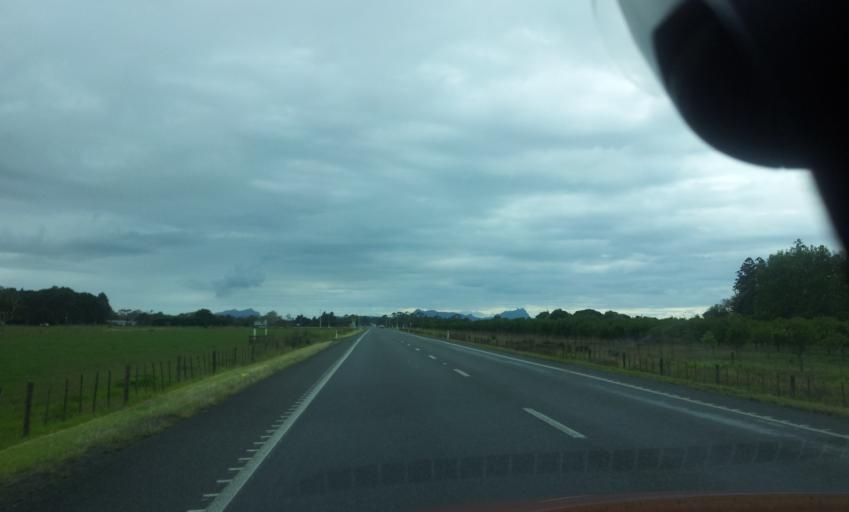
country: NZ
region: Northland
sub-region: Whangarei
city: Ruakaka
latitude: -35.9810
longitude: 174.4332
